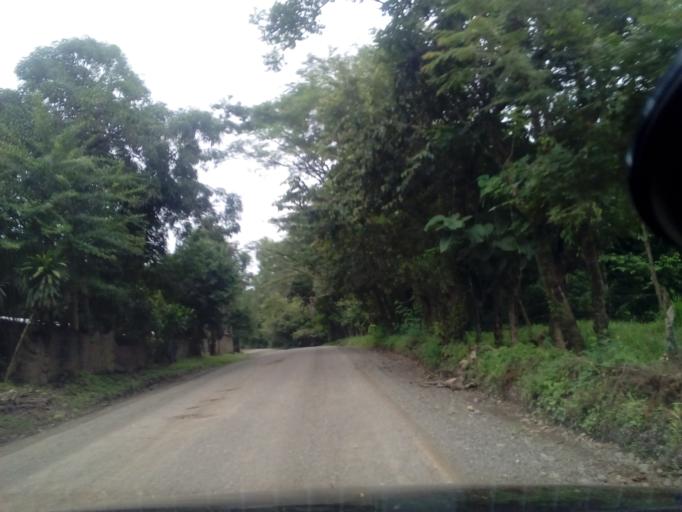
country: CR
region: Guanacaste
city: Samara
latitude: 9.9143
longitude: -85.5748
